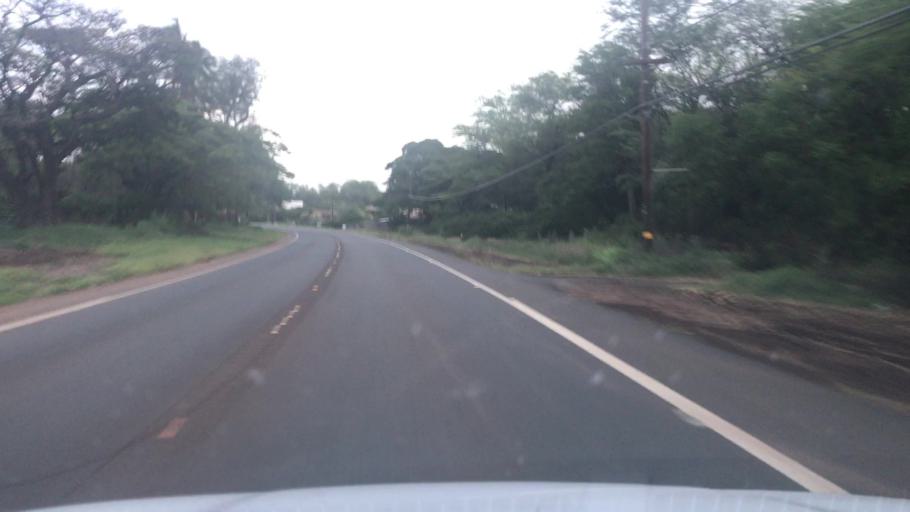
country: US
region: Hawaii
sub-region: Maui County
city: Kaunakakai
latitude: 21.0661
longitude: -156.9506
